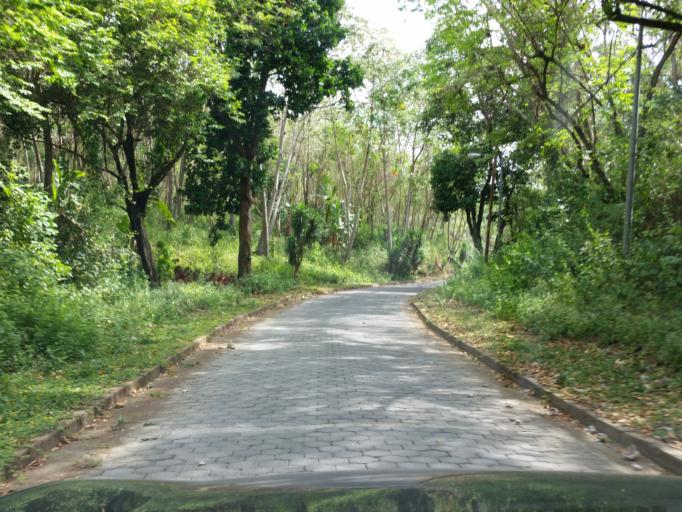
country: NI
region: Masaya
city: Ticuantepe
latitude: 12.0469
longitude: -86.2658
